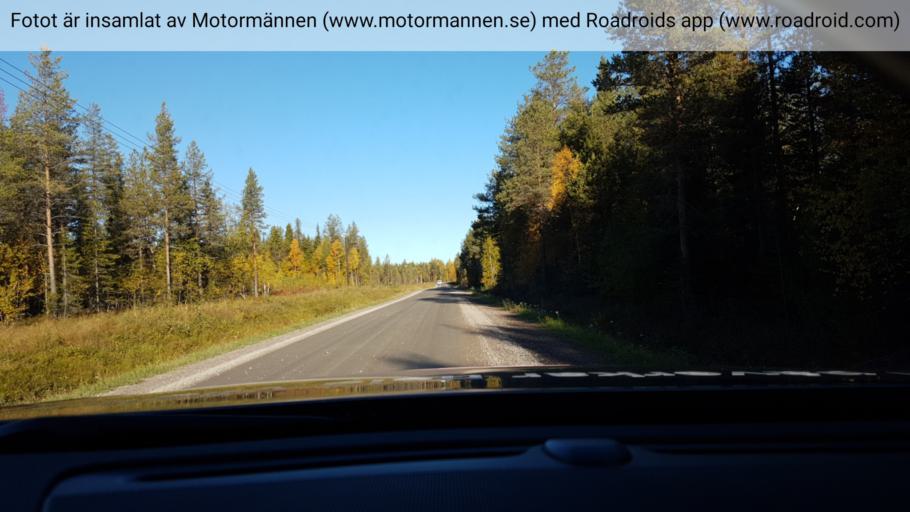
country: SE
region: Norrbotten
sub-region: Alvsbyns Kommun
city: AElvsbyn
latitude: 66.1643
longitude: 21.2505
